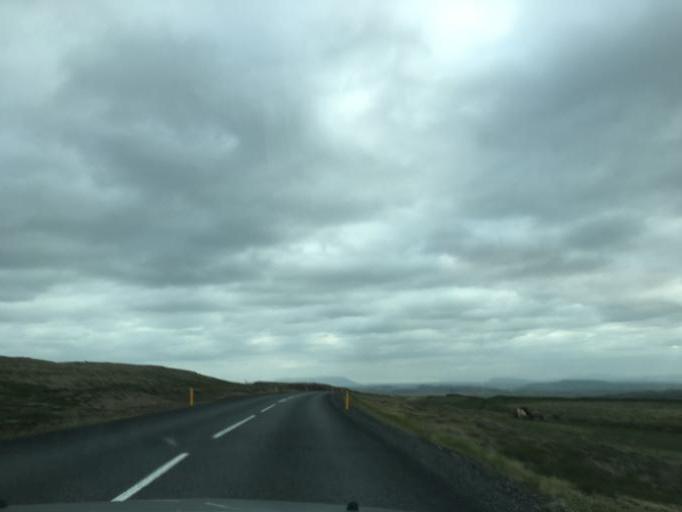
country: IS
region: South
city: Vestmannaeyjar
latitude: 64.2426
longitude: -20.2162
